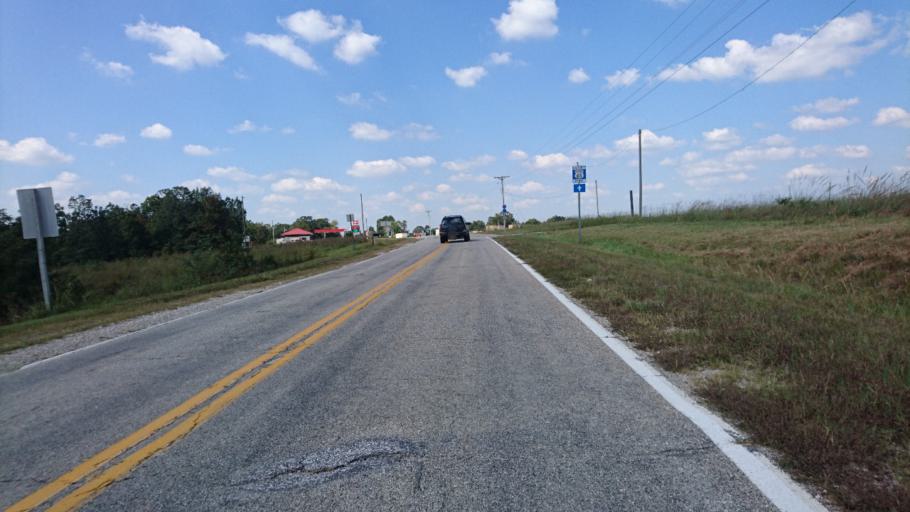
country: US
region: Missouri
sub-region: Pulaski County
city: Richland
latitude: 37.7538
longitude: -92.5053
